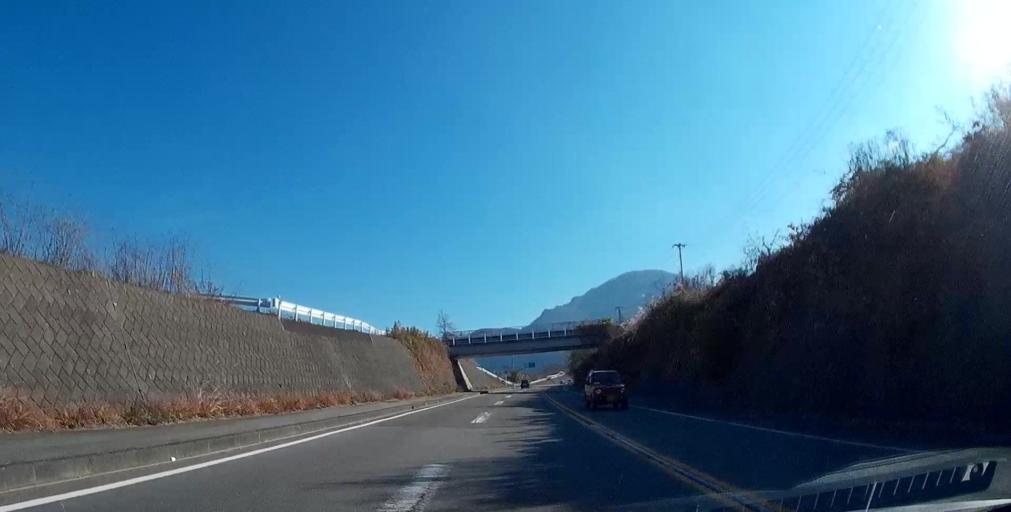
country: JP
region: Yamanashi
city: Isawa
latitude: 35.6032
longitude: 138.7059
